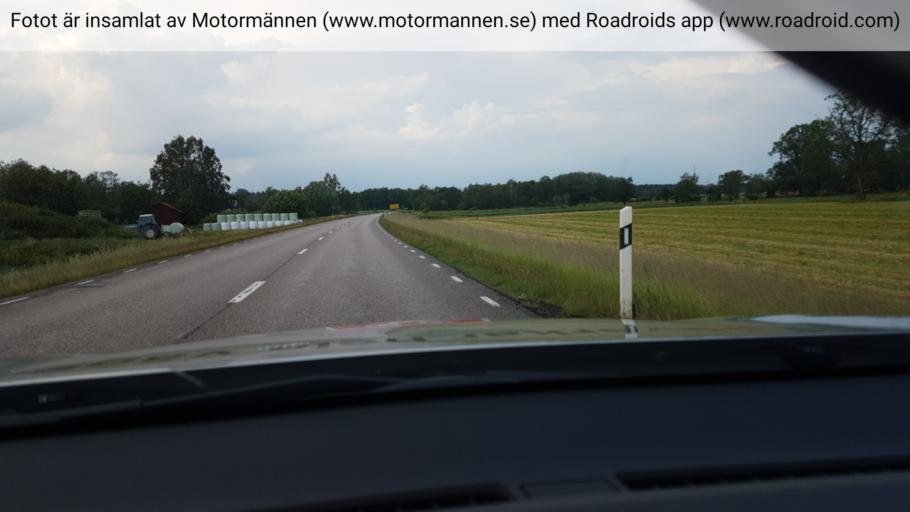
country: SE
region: Vaestra Goetaland
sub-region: Hjo Kommun
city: Hjo
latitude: 58.2135
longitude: 14.2048
